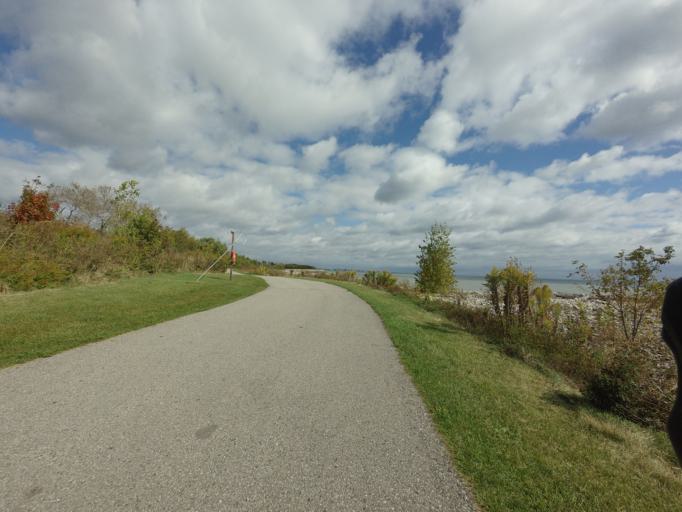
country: CA
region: Ontario
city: Scarborough
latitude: 43.7718
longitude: -79.1377
